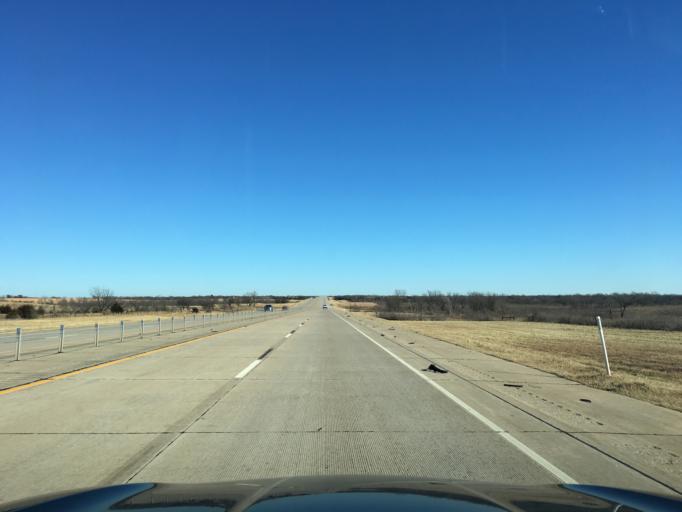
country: US
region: Oklahoma
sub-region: Payne County
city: Yale
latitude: 36.2249
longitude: -96.6956
